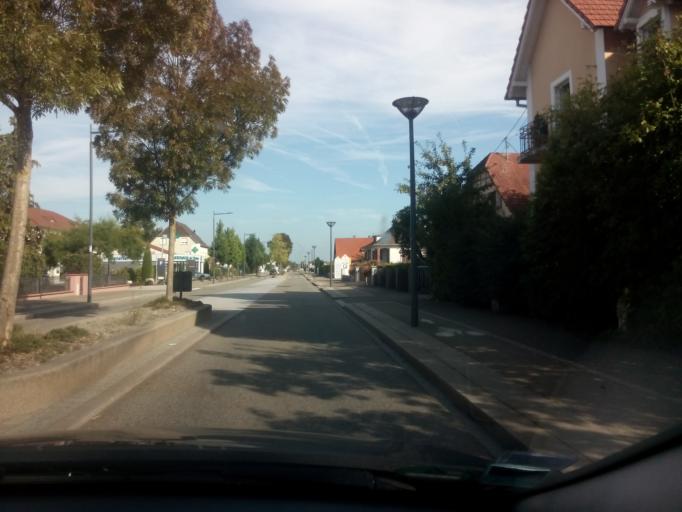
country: FR
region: Alsace
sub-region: Departement du Bas-Rhin
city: Wissembourg
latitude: 49.0304
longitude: 7.9563
